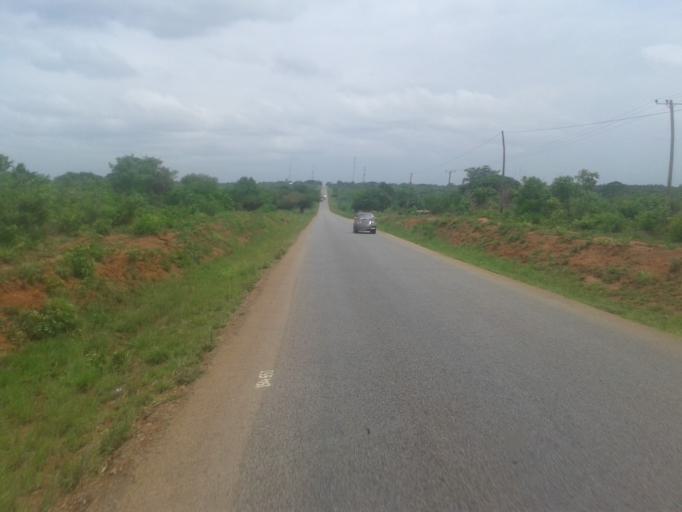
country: UG
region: Western Region
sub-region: Kiryandongo District
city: Masindi Port
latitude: 1.5020
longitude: 32.1183
